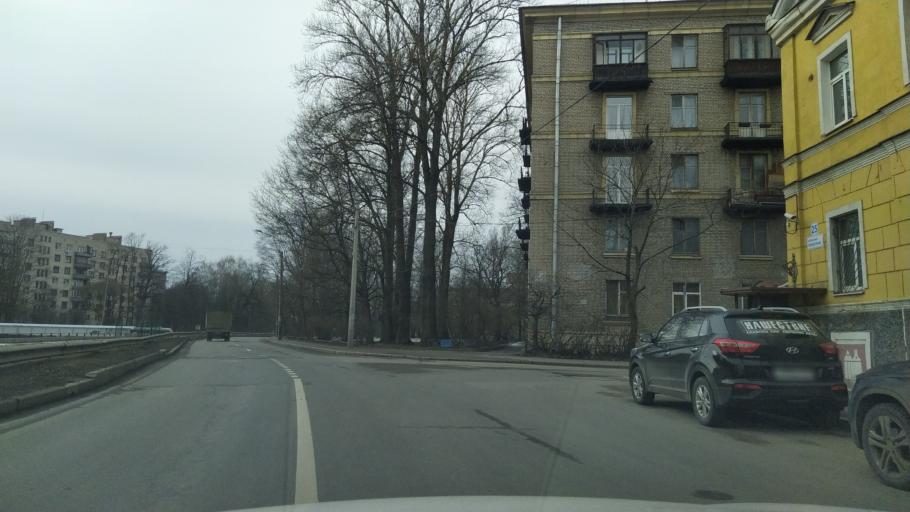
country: RU
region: Leningrad
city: Chernaya Rechka
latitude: 59.9846
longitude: 30.3140
